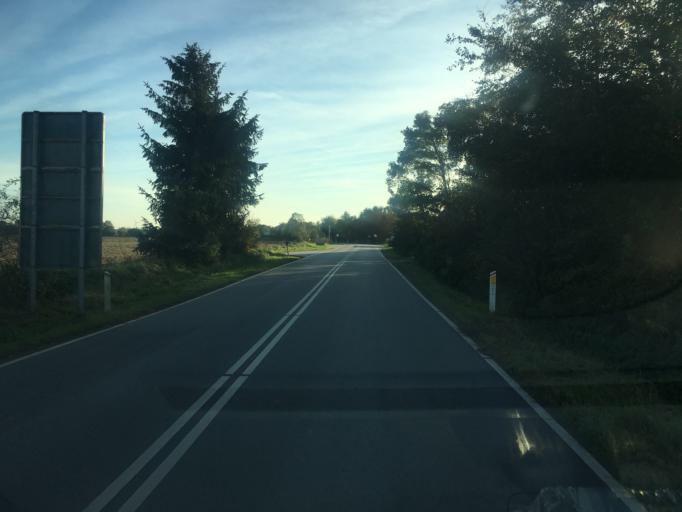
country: DE
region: Schleswig-Holstein
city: Bramstedtlund
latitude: 54.8733
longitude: 9.0800
